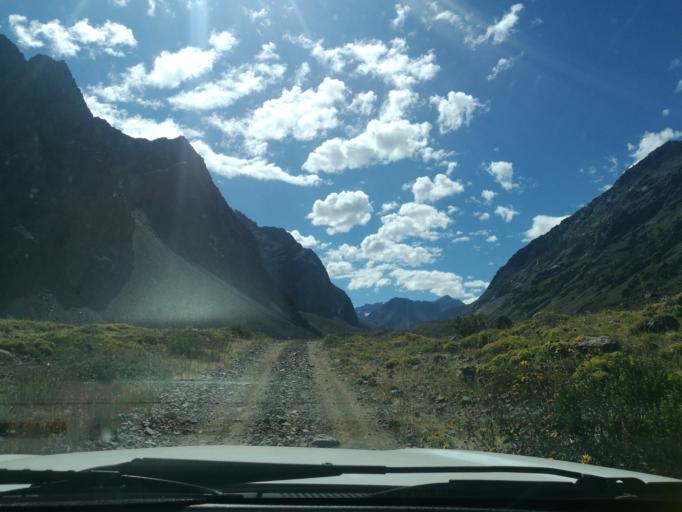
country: CL
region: O'Higgins
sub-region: Provincia de Cachapoal
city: Machali
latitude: -34.4089
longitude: -70.2410
